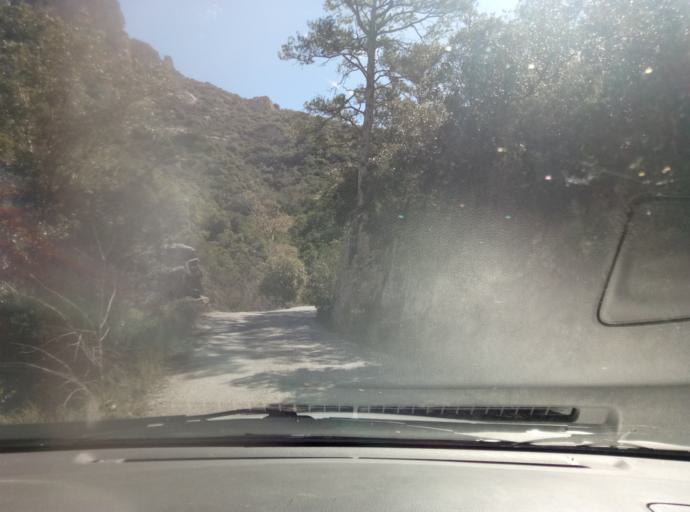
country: ES
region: Catalonia
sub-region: Provincia de Tarragona
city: Vimbodi
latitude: 41.3548
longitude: 1.0617
